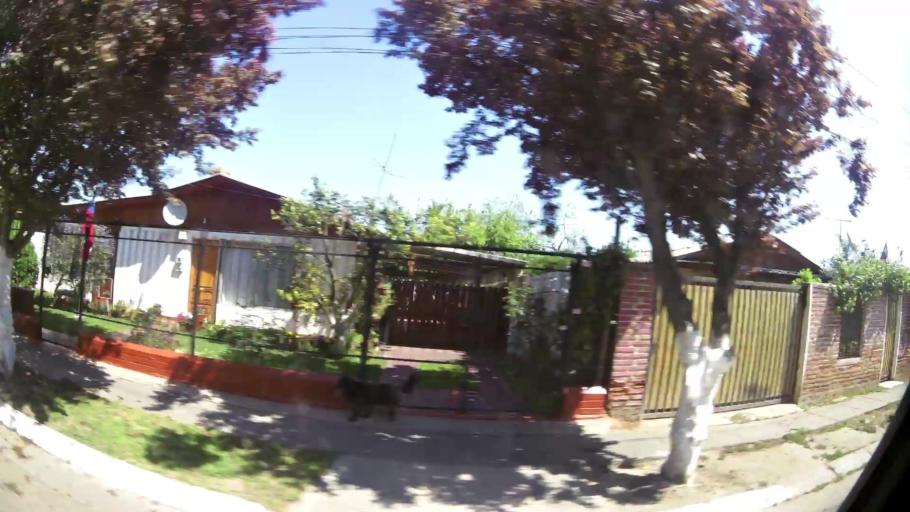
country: CL
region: Santiago Metropolitan
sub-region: Provincia de Talagante
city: Penaflor
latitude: -33.5723
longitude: -70.8094
